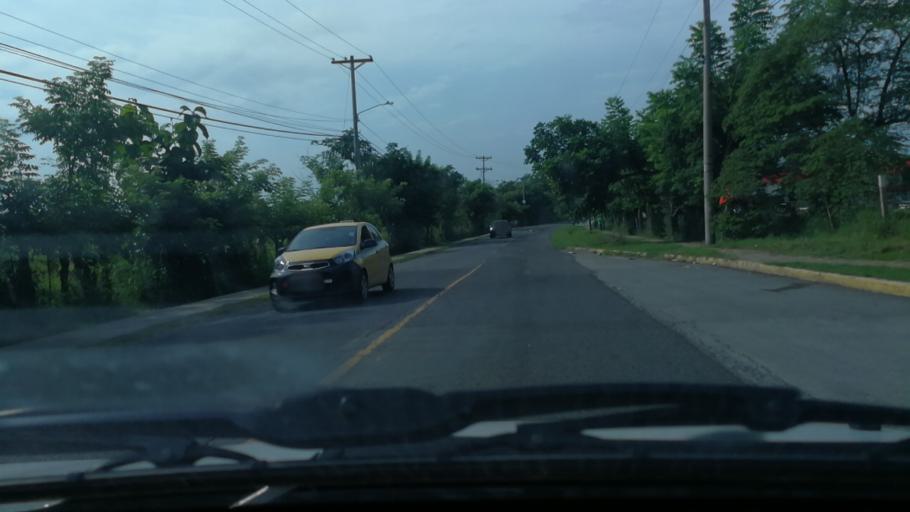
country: PA
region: Panama
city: Pacora
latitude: 9.0887
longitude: -79.2881
